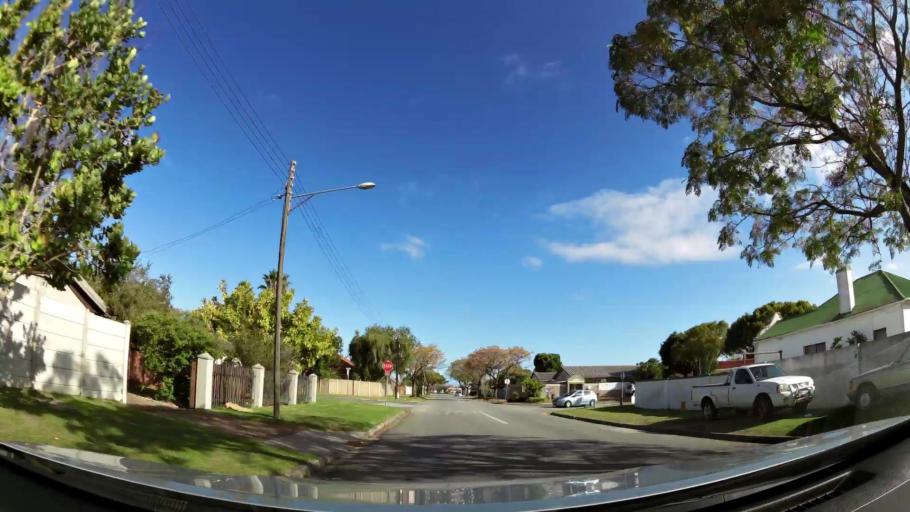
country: ZA
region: Western Cape
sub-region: Eden District Municipality
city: George
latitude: -33.9606
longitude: 22.4776
